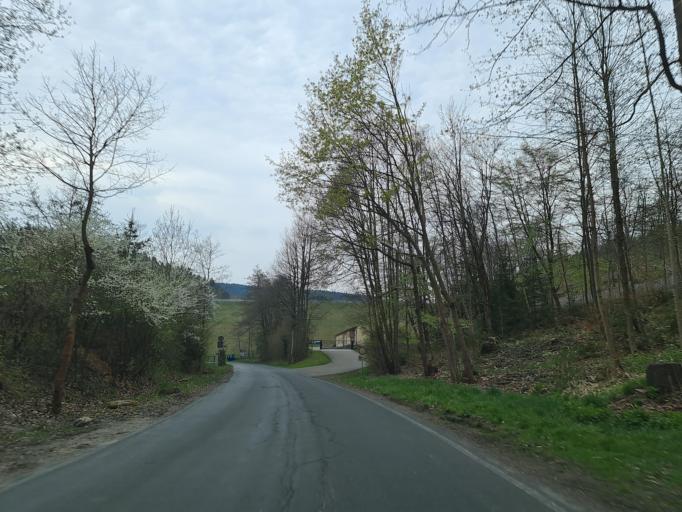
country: DE
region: Saxony
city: Falkenstein
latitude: 50.4695
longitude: 12.3770
